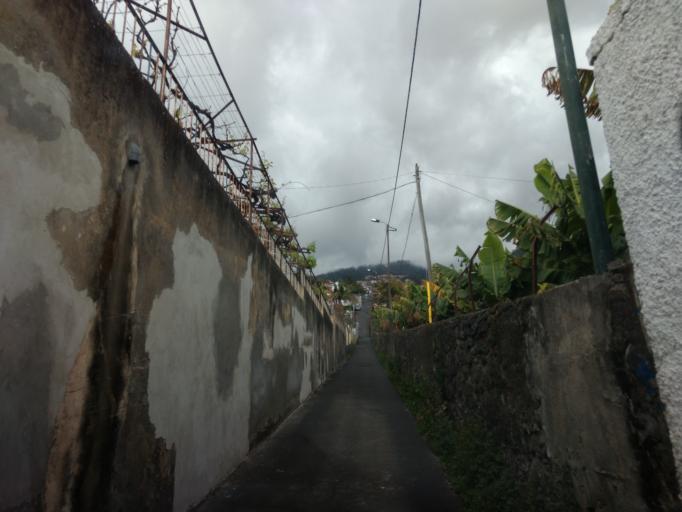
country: PT
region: Madeira
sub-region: Funchal
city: Nossa Senhora do Monte
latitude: 32.6657
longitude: -16.9346
